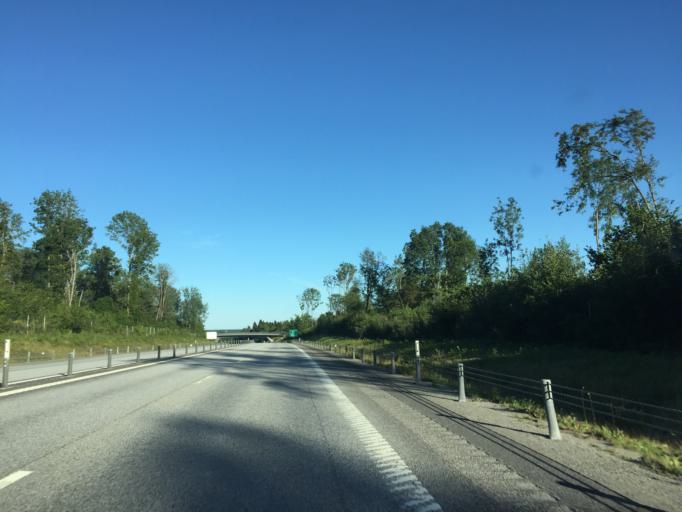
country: SE
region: OErebro
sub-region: Orebro Kommun
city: Vintrosa
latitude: 59.2484
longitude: 14.9291
